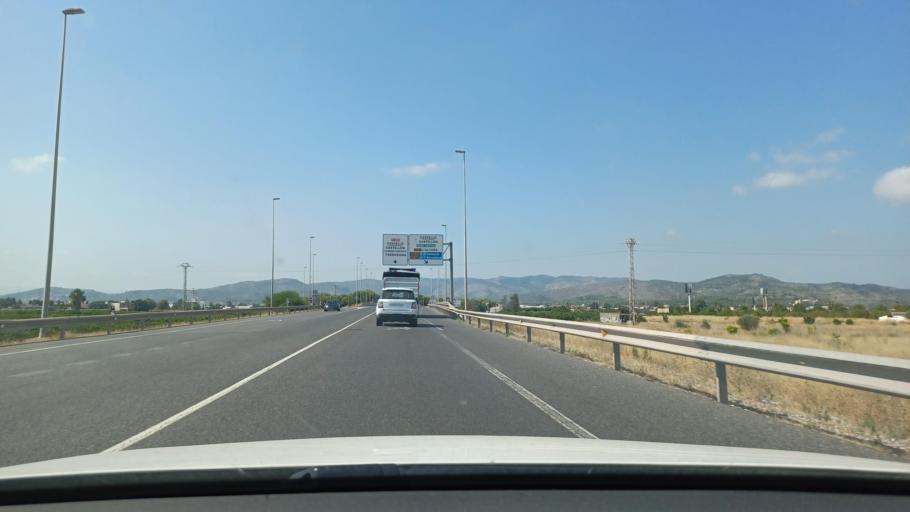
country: ES
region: Valencia
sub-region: Provincia de Castello
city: Almassora
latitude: 39.9795
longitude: -0.0872
